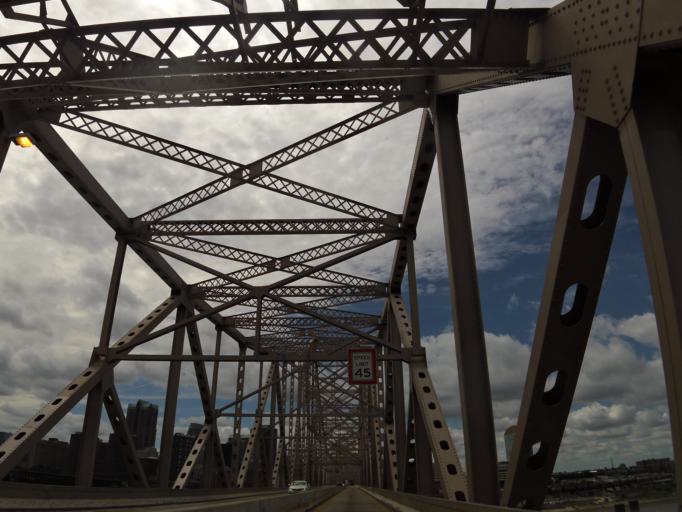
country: US
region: Missouri
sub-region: City of Saint Louis
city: St. Louis
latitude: 38.6308
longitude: -90.1761
